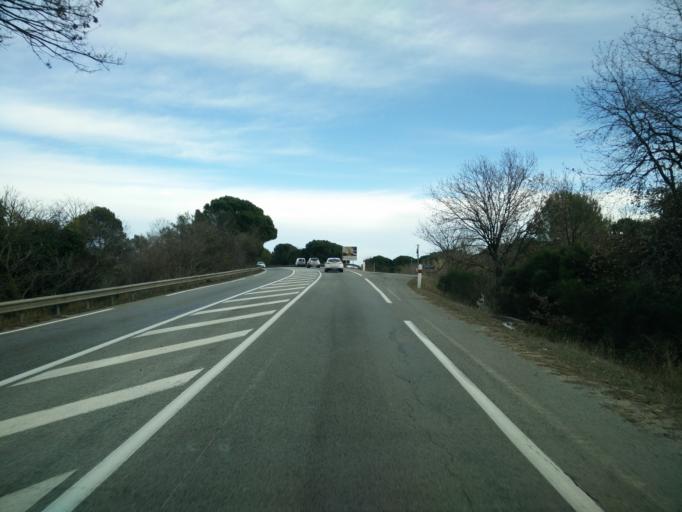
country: FR
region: Provence-Alpes-Cote d'Azur
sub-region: Departement du Var
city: Les Arcs
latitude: 43.4540
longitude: 6.5084
